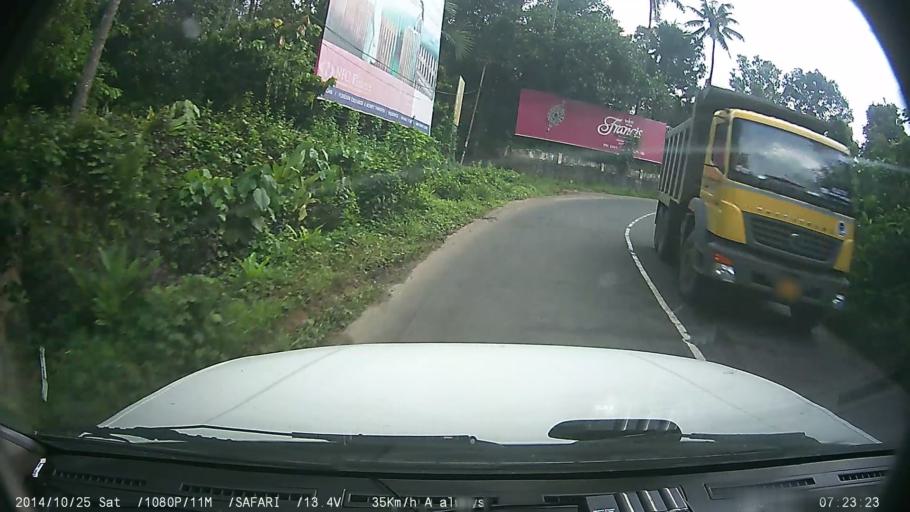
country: IN
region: Kerala
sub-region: Kottayam
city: Palackattumala
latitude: 9.7922
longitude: 76.5771
